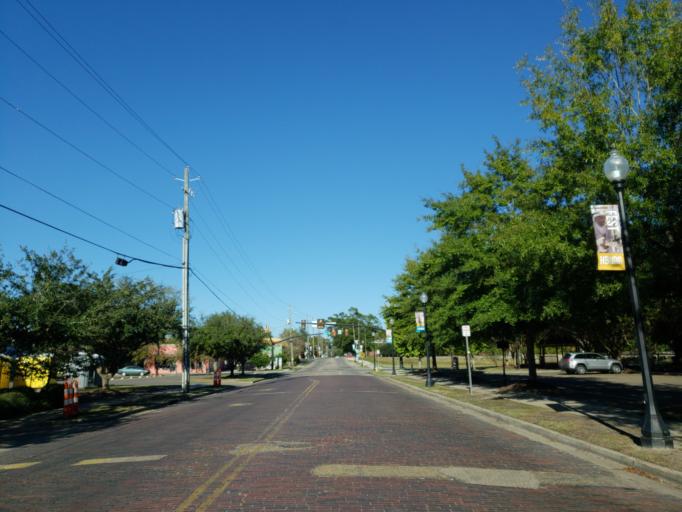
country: US
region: Mississippi
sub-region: Forrest County
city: Hattiesburg
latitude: 31.3242
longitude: -89.2883
